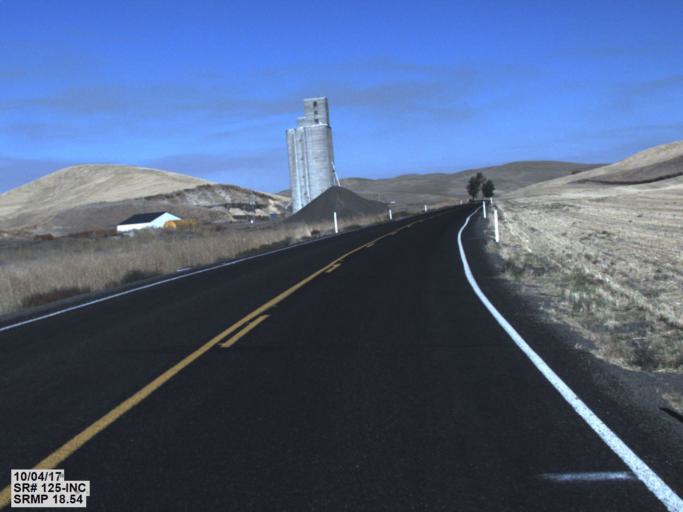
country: US
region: Washington
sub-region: Walla Walla County
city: Walla Walla
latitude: 46.2317
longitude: -118.3783
